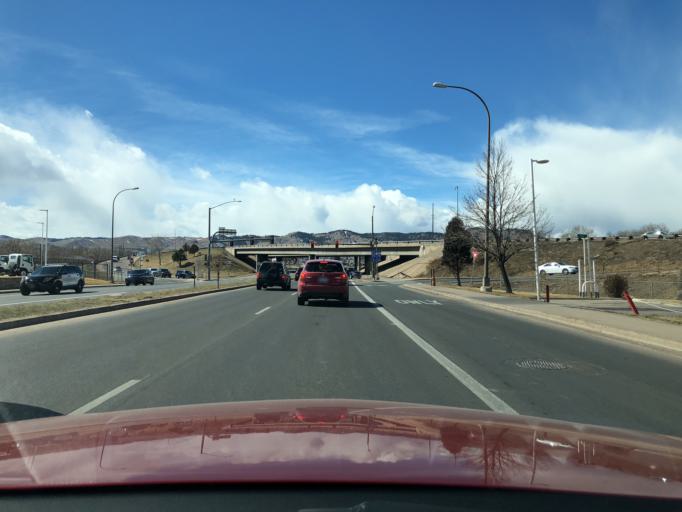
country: US
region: Colorado
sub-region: Jefferson County
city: West Pleasant View
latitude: 39.7316
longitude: -105.1682
